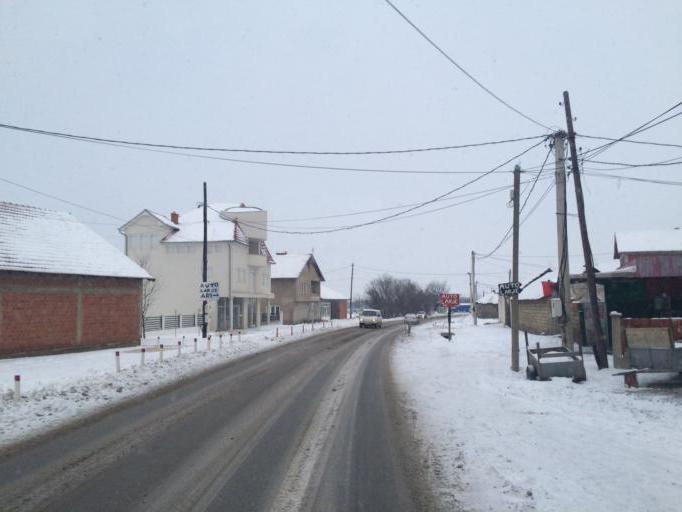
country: XK
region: Pristina
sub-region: Komuna e Drenasit
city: Glogovac
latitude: 42.5872
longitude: 20.8946
